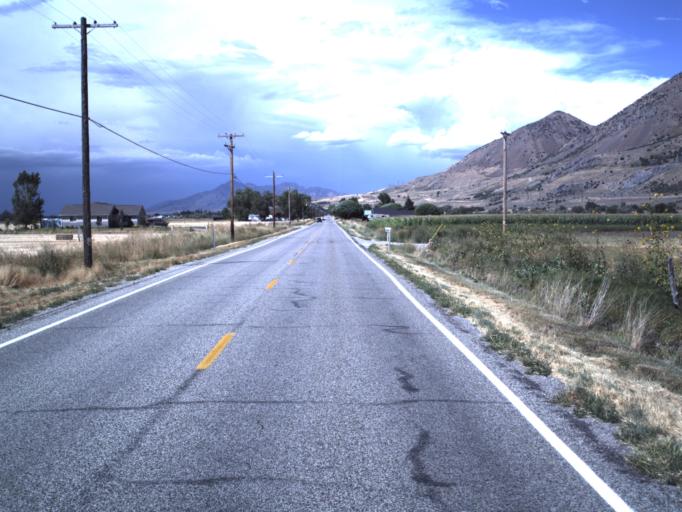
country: US
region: Utah
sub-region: Box Elder County
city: Honeyville
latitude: 41.6782
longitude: -112.0898
